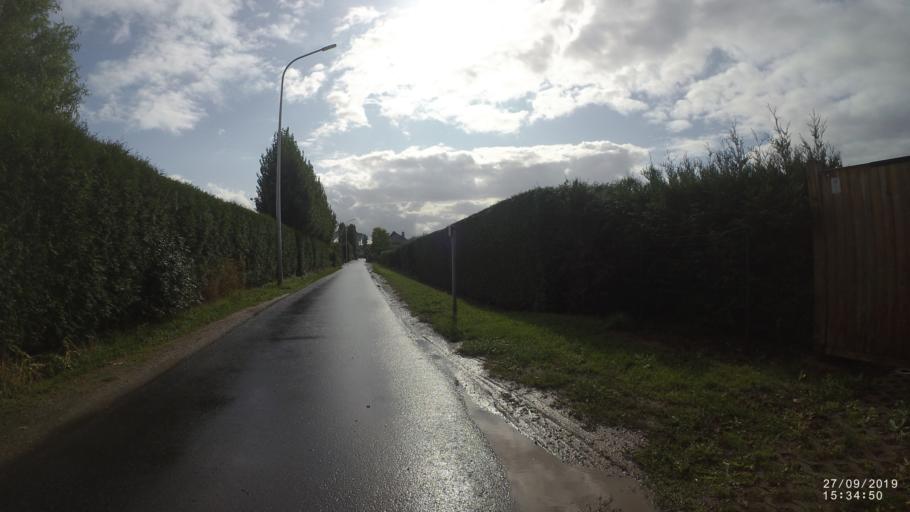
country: BE
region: Flanders
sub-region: Provincie Oost-Vlaanderen
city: Zottegem
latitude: 50.8779
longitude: 3.7414
